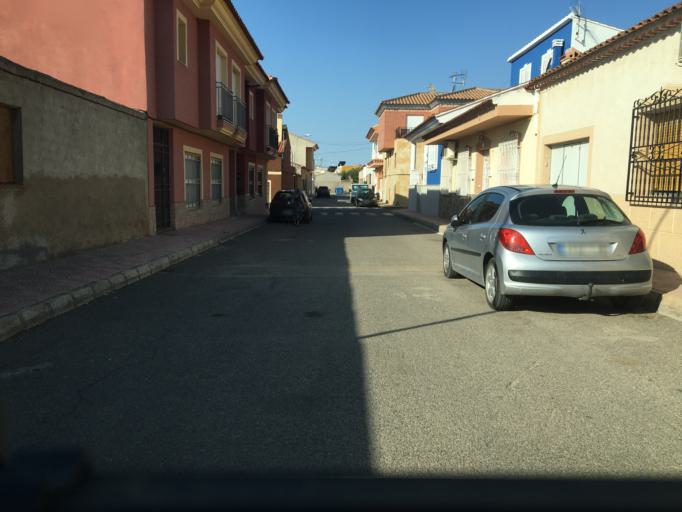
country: ES
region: Murcia
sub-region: Murcia
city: Puerto Lumbreras
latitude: 37.5534
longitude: -1.8159
